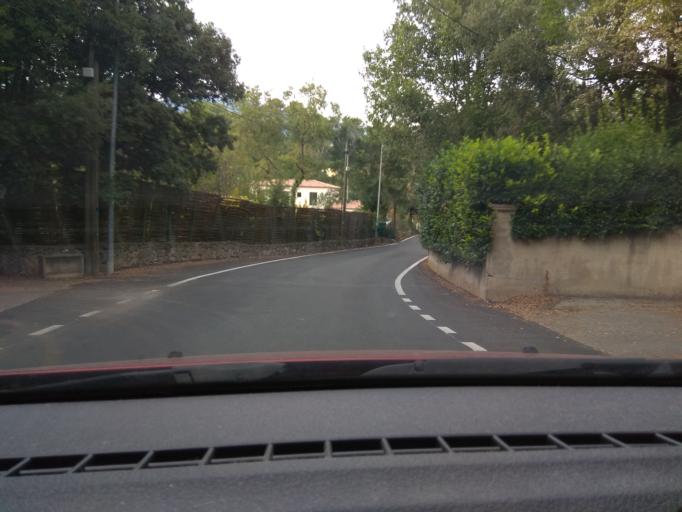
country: FR
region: Provence-Alpes-Cote d'Azur
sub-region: Departement des Alpes-Maritimes
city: Le Rouret
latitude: 43.6773
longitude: 7.0455
